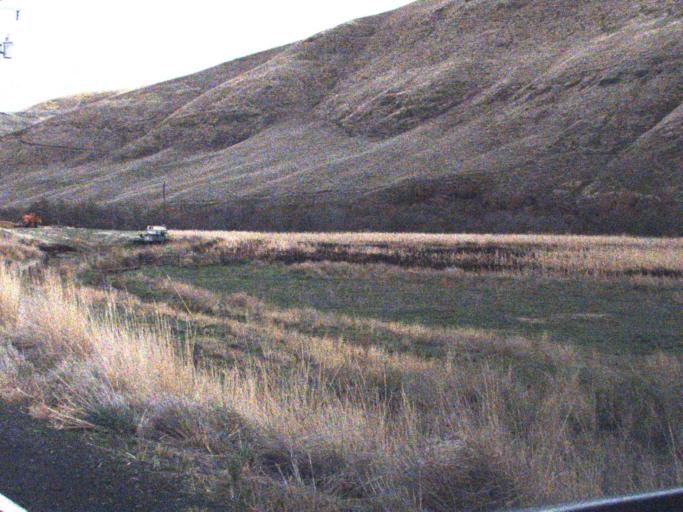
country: US
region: Washington
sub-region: Columbia County
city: Dayton
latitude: 46.5094
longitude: -118.0885
